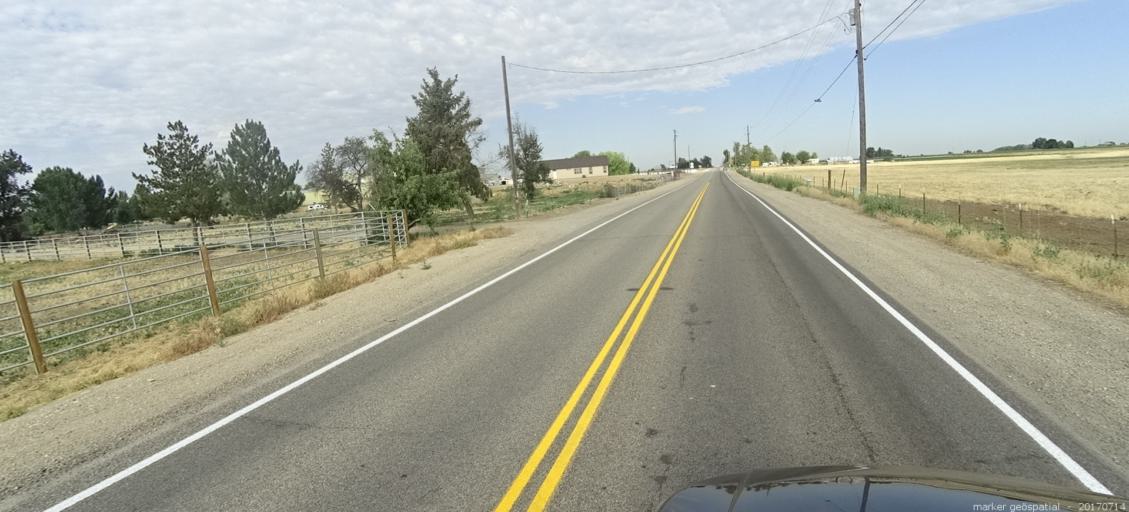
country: US
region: Idaho
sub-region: Ada County
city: Kuna
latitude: 43.4884
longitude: -116.4343
